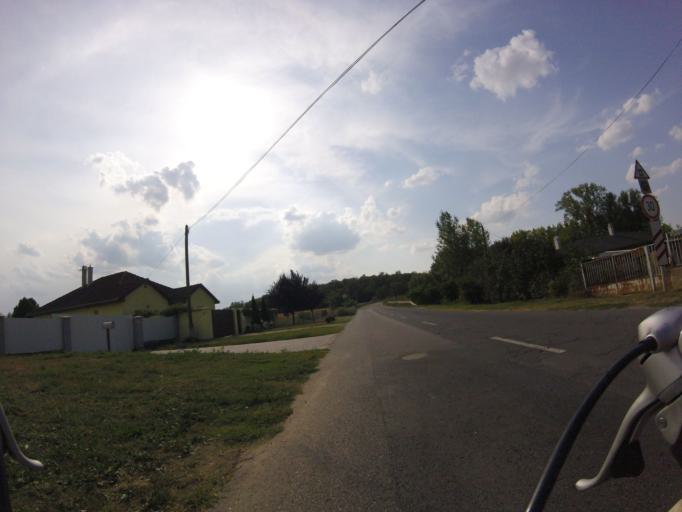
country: HU
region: Szabolcs-Szatmar-Bereg
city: Kotaj
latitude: 48.0292
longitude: 21.7589
